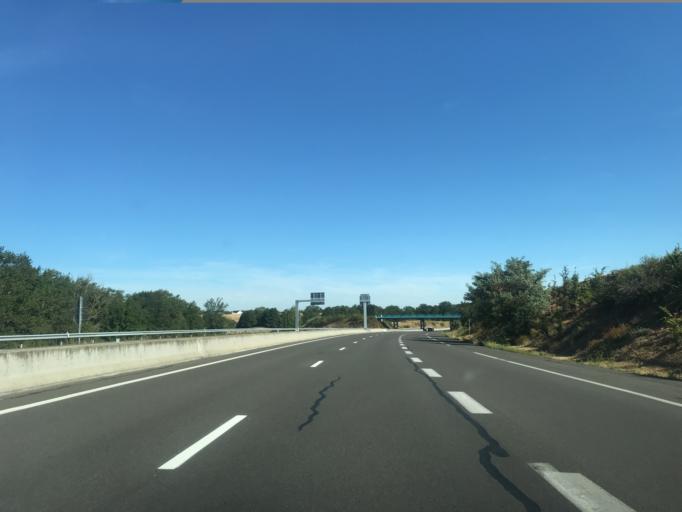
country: FR
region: Auvergne
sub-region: Departement de l'Allier
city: Premilhat
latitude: 46.3351
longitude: 2.5361
